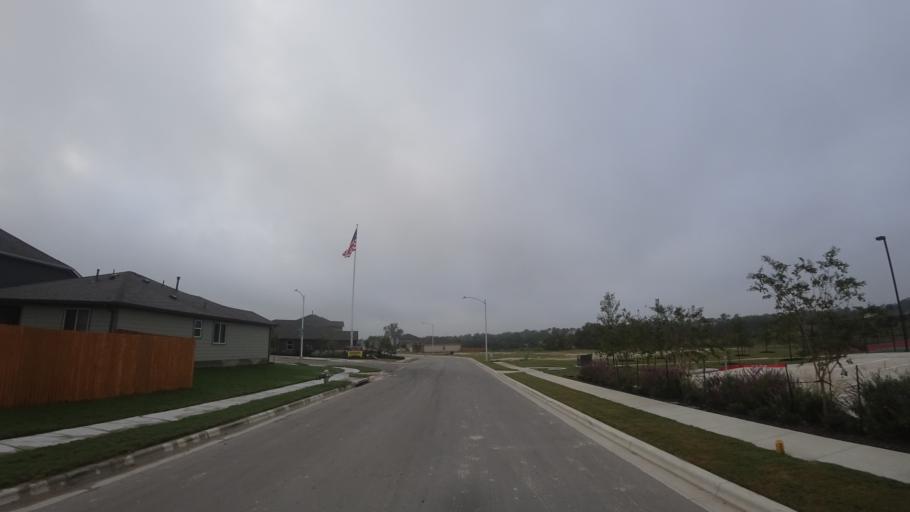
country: US
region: Texas
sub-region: Travis County
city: Wells Branch
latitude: 30.3580
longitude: -97.6655
